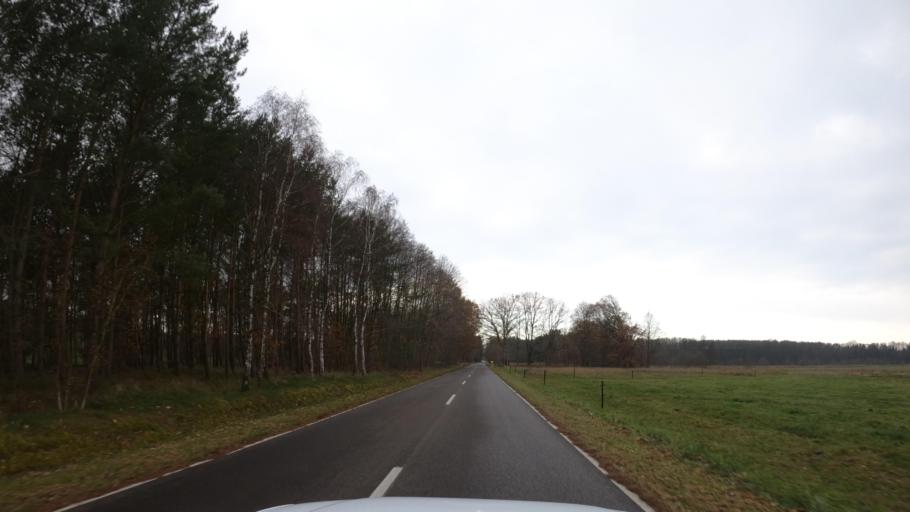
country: PL
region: West Pomeranian Voivodeship
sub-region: Powiat policki
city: Nowe Warpno
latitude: 53.6977
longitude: 14.3454
